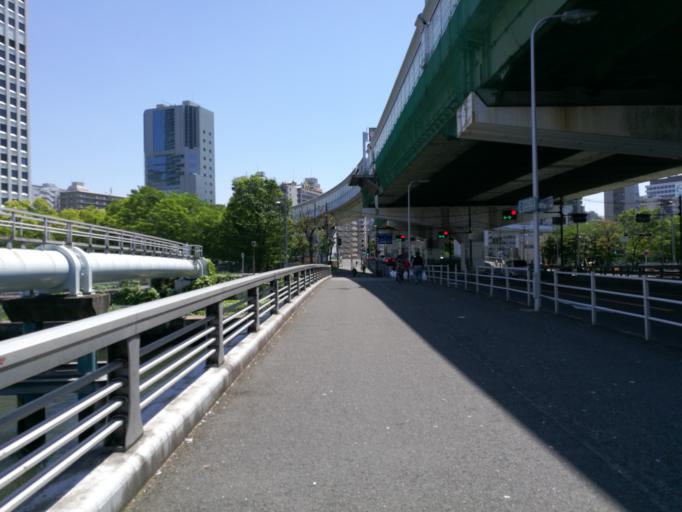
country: JP
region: Osaka
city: Osaka-shi
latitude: 34.6871
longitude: 135.4824
